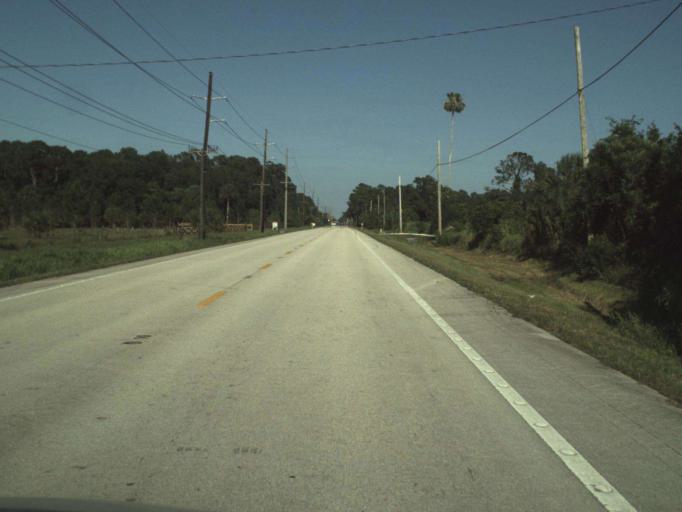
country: US
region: Florida
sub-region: Brevard County
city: Mims
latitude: 28.6655
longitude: -80.9234
